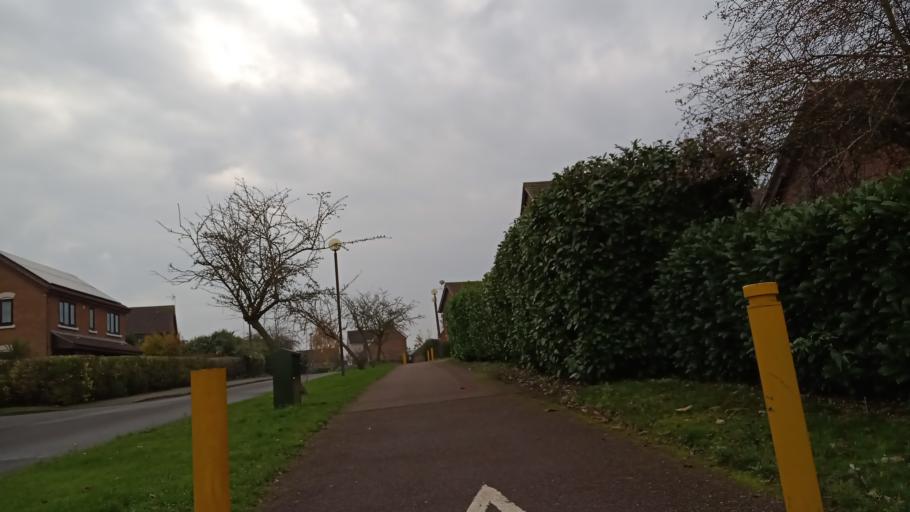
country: GB
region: England
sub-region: Milton Keynes
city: Shenley Church End
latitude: 52.0101
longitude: -0.7862
